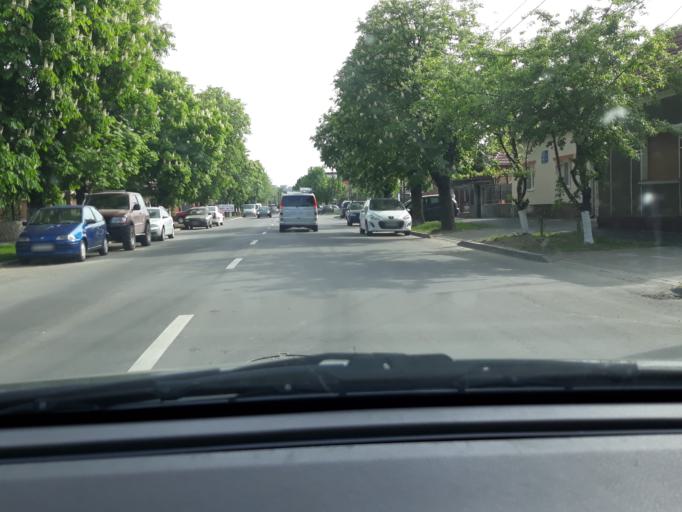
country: RO
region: Bihor
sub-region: Comuna Biharea
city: Oradea
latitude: 47.0427
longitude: 21.9559
